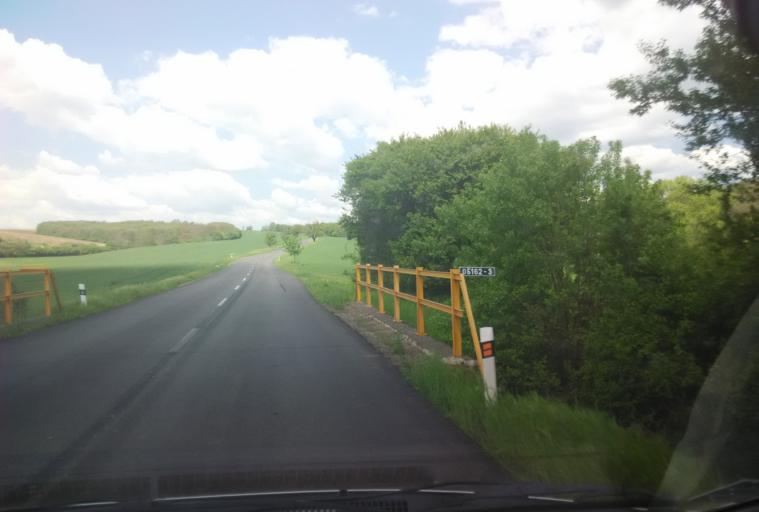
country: SK
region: Banskobystricky
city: Dudince
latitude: 48.2088
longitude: 18.7895
